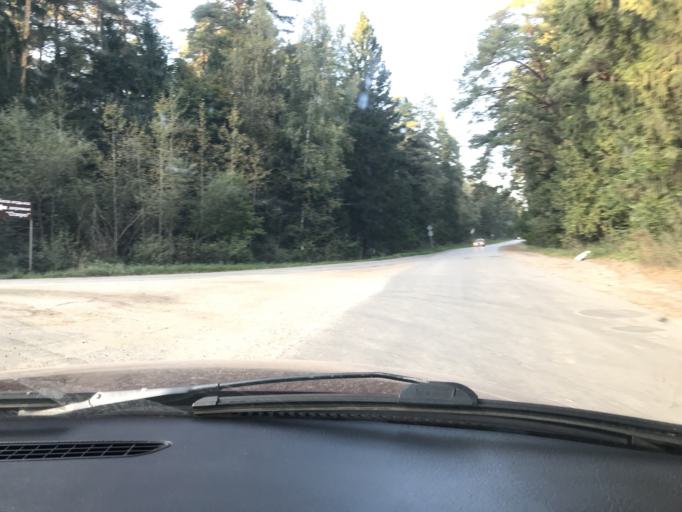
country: RU
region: Kaluga
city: Kondrovo
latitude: 54.7808
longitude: 35.9108
